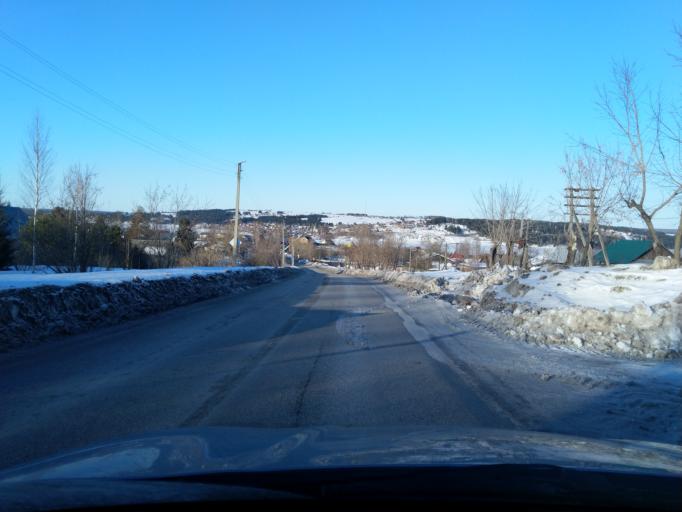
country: RU
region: Perm
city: Polazna
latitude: 58.2928
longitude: 56.4152
